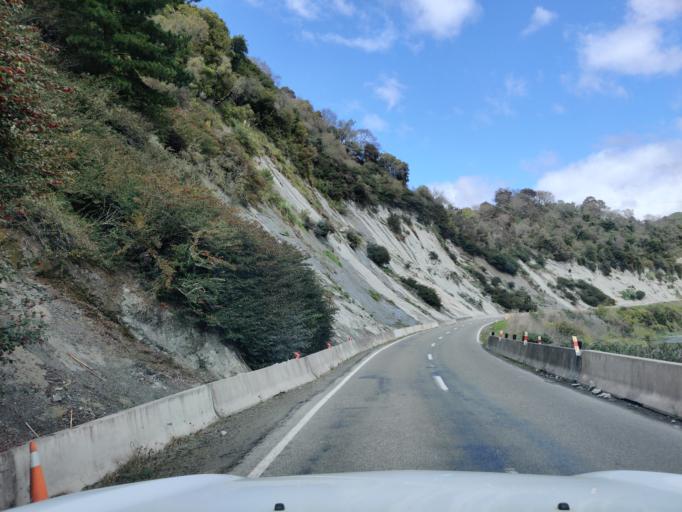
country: NZ
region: Manawatu-Wanganui
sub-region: Ruapehu District
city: Waiouru
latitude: -39.6444
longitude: 175.3269
